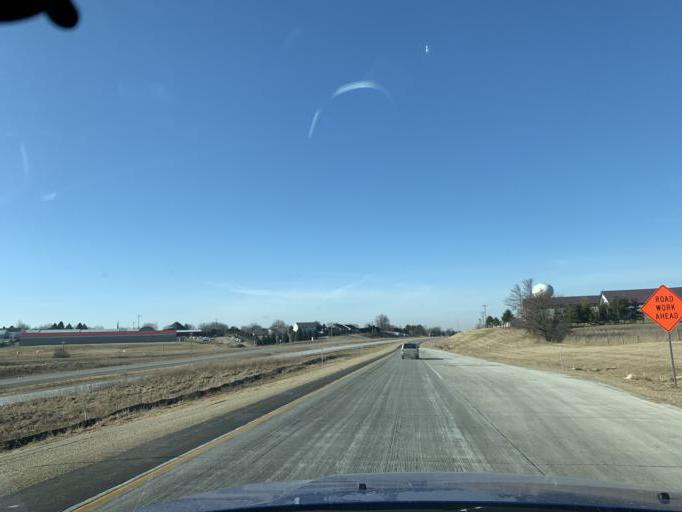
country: US
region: Wisconsin
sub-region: Green County
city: Monroe
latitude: 42.6089
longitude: -89.6191
